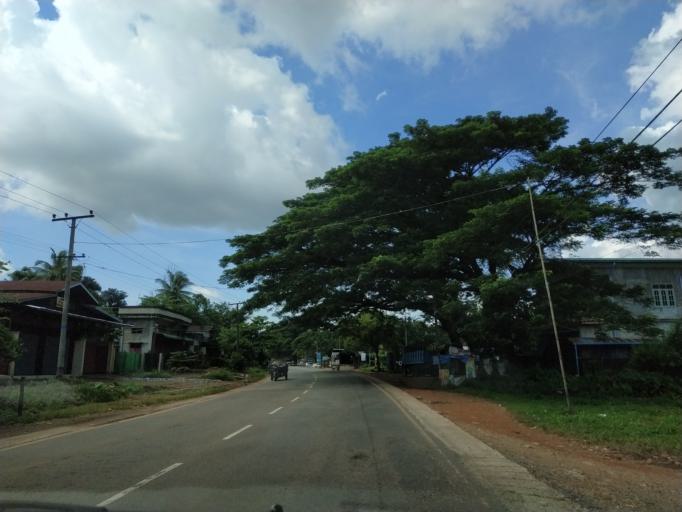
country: MM
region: Mon
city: Kyaikkami
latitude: 15.9492
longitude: 97.7312
